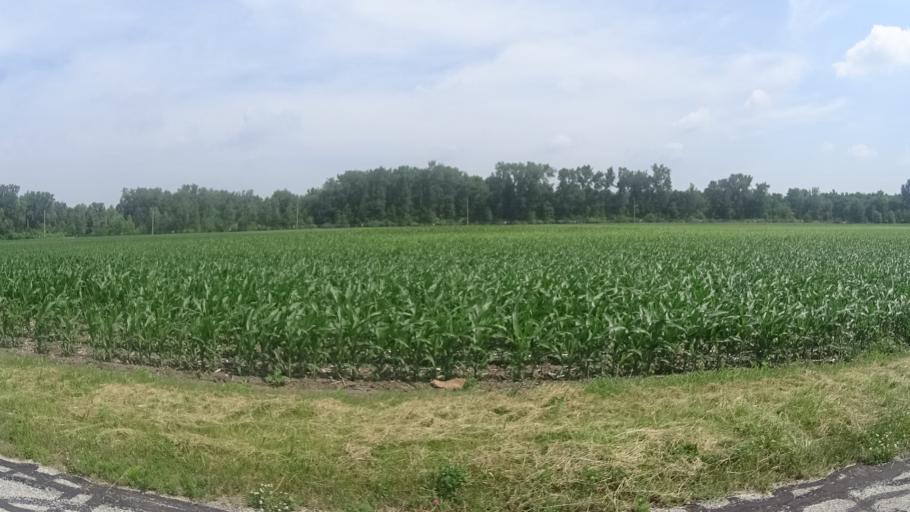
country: US
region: Ohio
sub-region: Erie County
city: Sandusky
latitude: 41.3600
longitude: -82.6977
